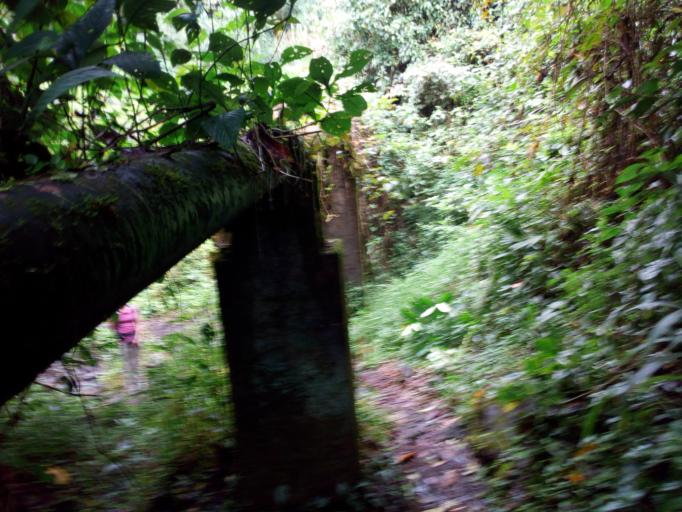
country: CM
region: South-West Province
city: Buea
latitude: 4.1625
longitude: 9.2237
